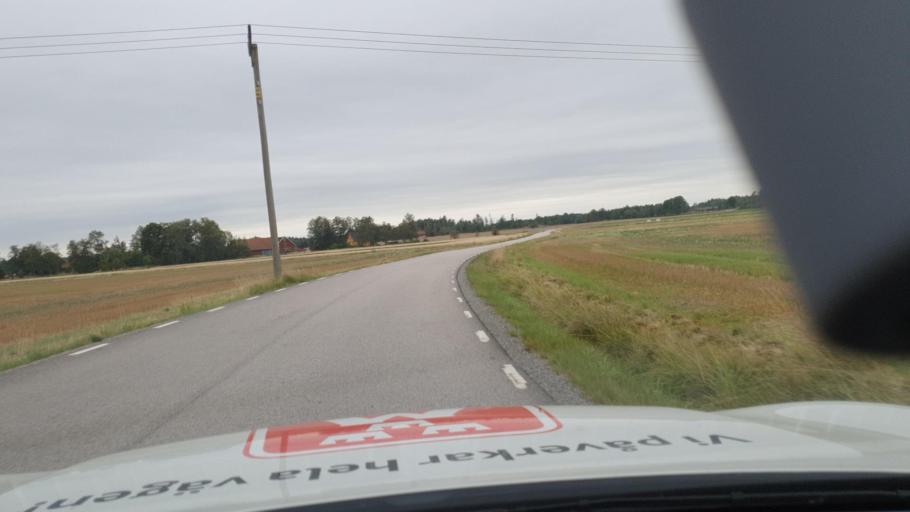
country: SE
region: Vaestra Goetaland
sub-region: Vanersborgs Kommun
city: Vanersborg
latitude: 58.4944
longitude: 12.2554
